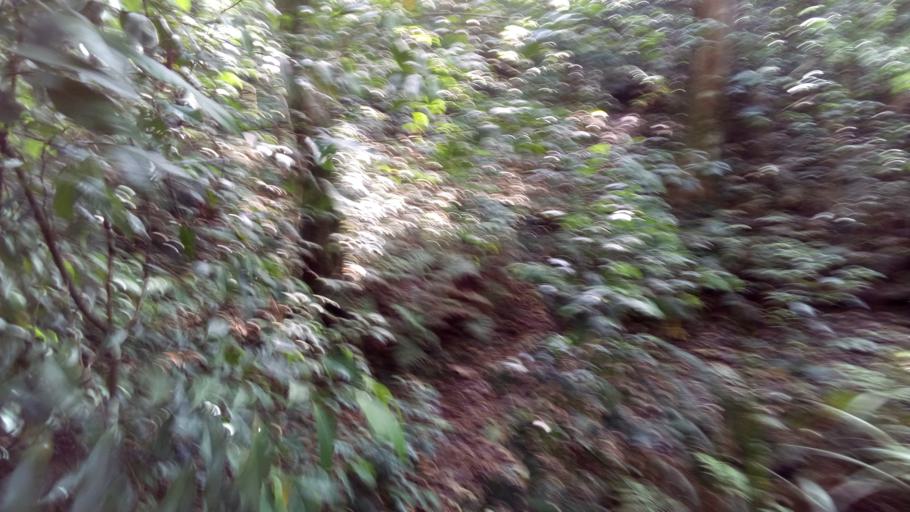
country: AU
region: New South Wales
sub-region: Wollongong
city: Mangerton
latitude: -34.4334
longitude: 150.8740
